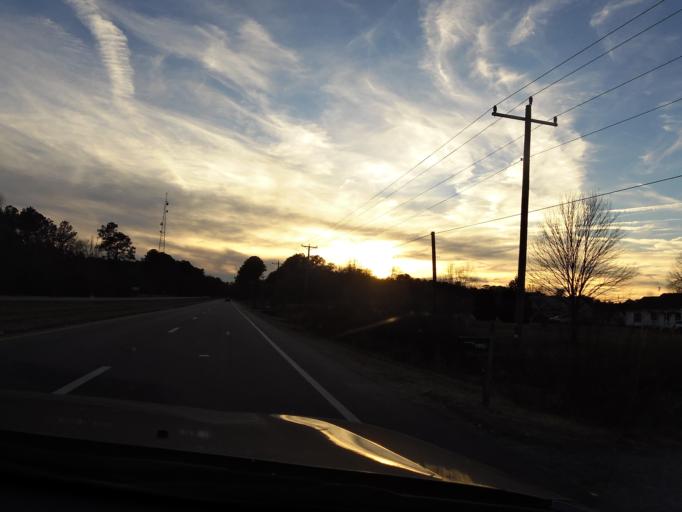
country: US
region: Virginia
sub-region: City of Franklin
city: Franklin
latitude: 36.6879
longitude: -76.9949
